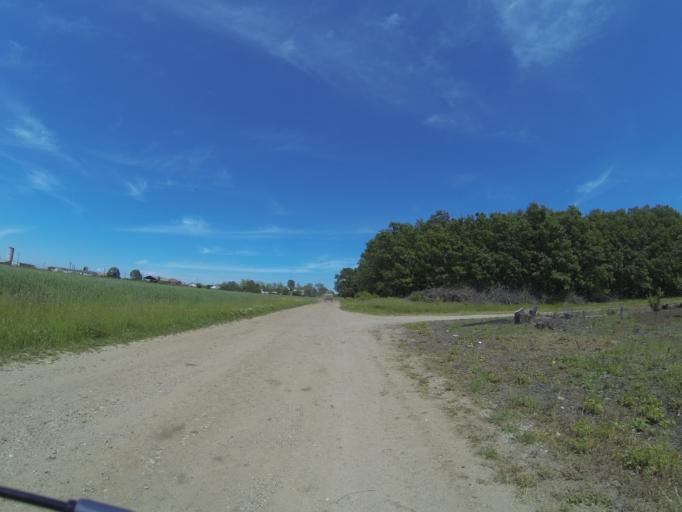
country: RO
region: Dolj
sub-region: Comuna Teslui
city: Teslui
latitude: 44.1679
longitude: 24.1612
